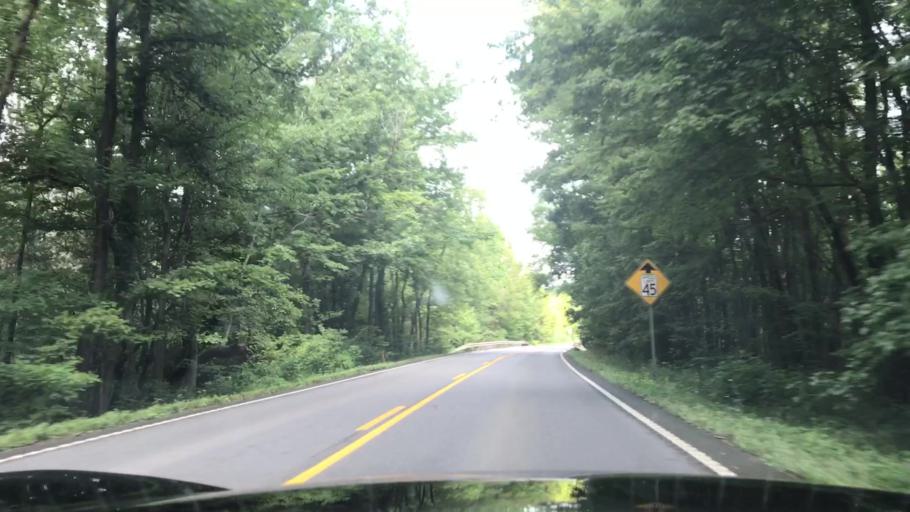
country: US
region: Kentucky
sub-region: Muhlenberg County
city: Central City
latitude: 37.2114
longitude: -87.0435
